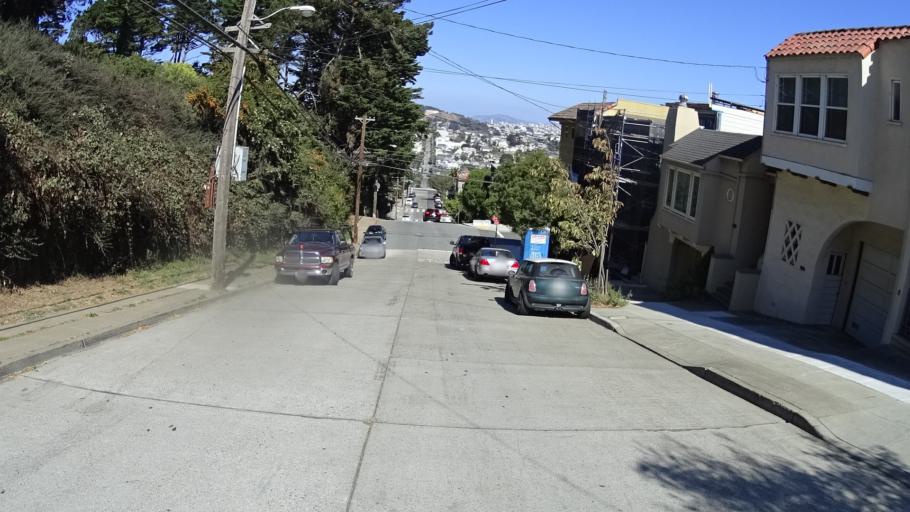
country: US
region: California
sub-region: San Francisco County
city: San Francisco
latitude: 37.7466
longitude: -122.4381
